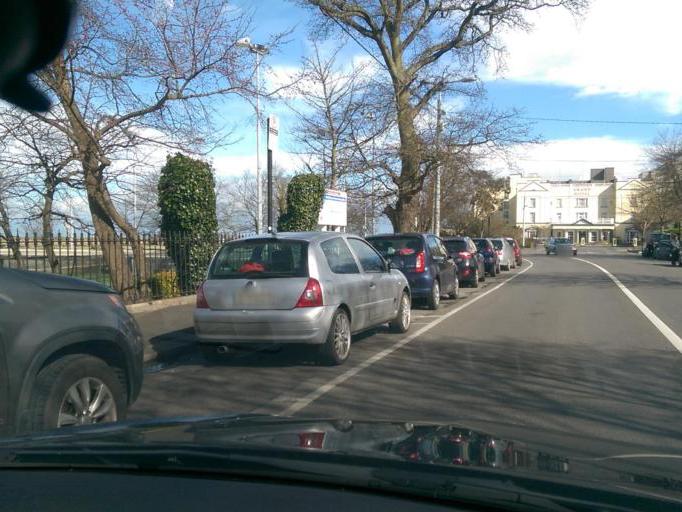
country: IE
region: Leinster
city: Malahide
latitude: 53.4510
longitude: -6.1504
